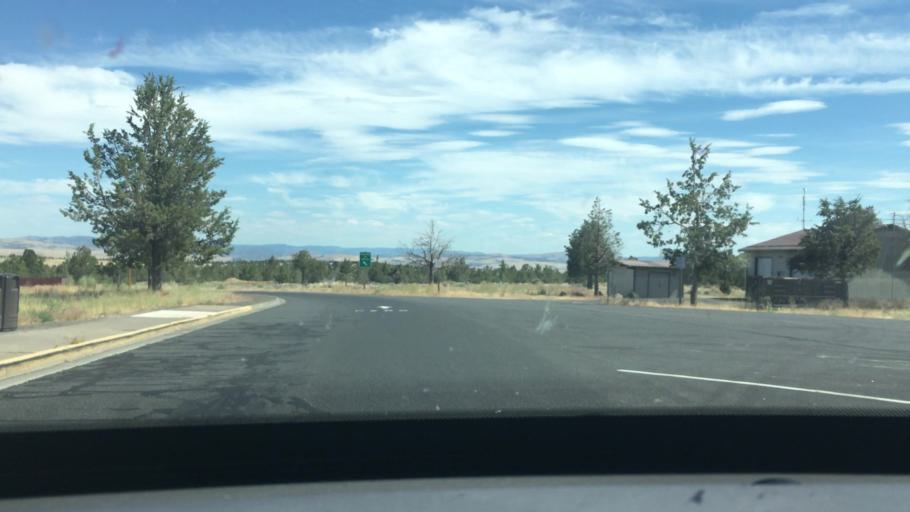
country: US
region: Oregon
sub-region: Jefferson County
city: Madras
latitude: 44.8943
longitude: -120.9364
